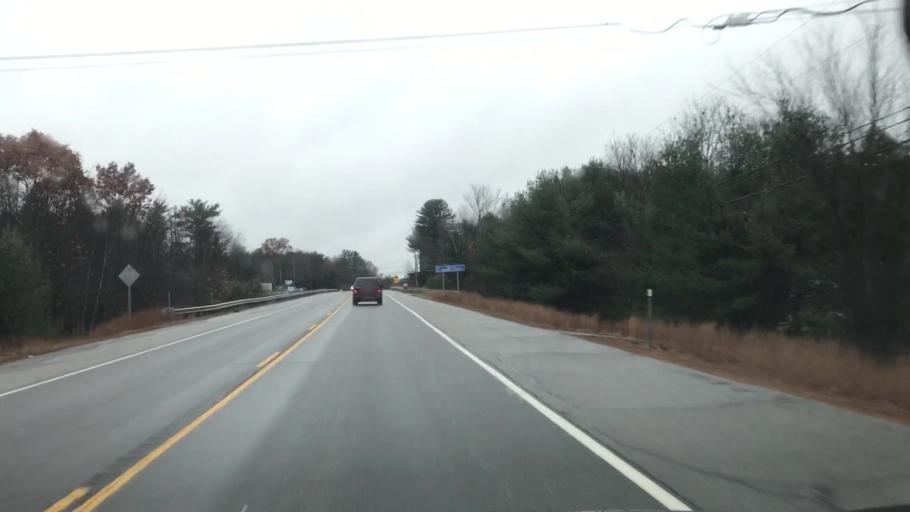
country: US
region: New Hampshire
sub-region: Merrimack County
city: Pittsfield
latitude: 43.2828
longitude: -71.3621
